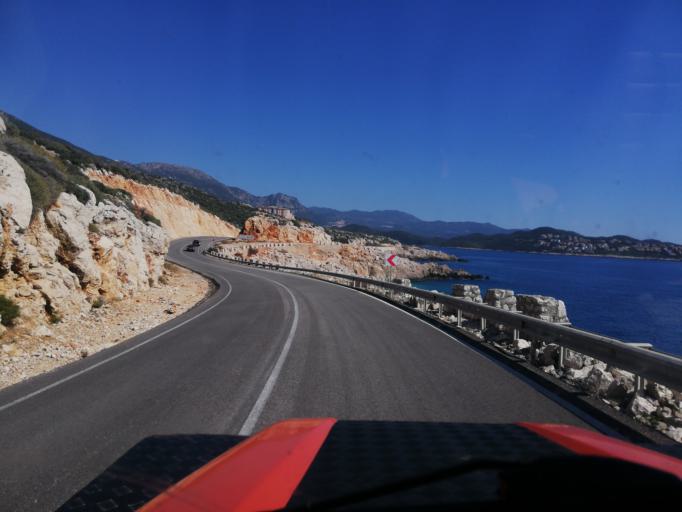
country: GR
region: South Aegean
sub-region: Nomos Dodekanisou
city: Megisti
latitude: 36.2029
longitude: 29.5741
